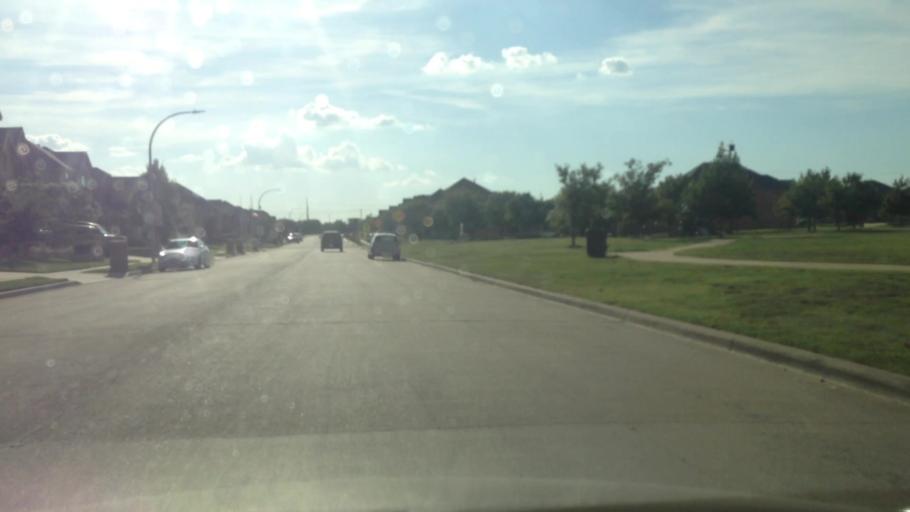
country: US
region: Texas
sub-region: Tarrant County
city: Haslet
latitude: 32.9375
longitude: -97.3881
